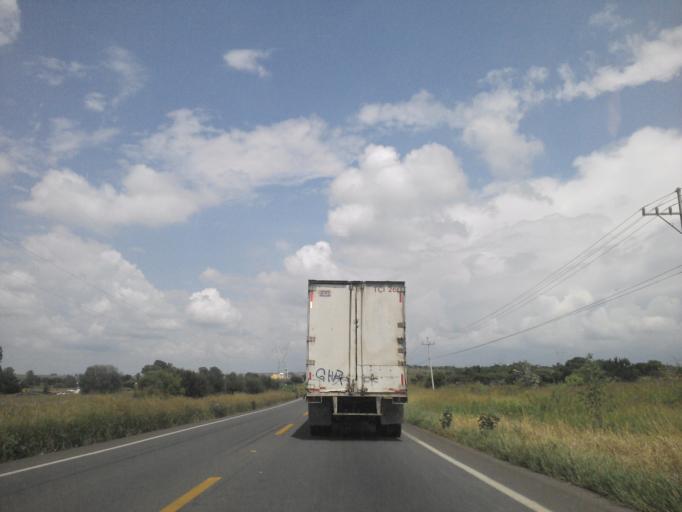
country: MX
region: Jalisco
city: Acatic
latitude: 20.7055
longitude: -102.9622
